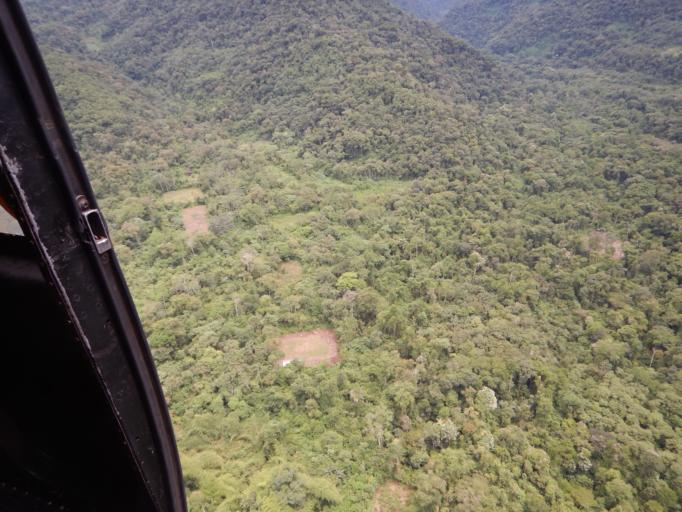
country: BO
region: Cochabamba
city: Totora
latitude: -17.4840
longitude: -64.9922
